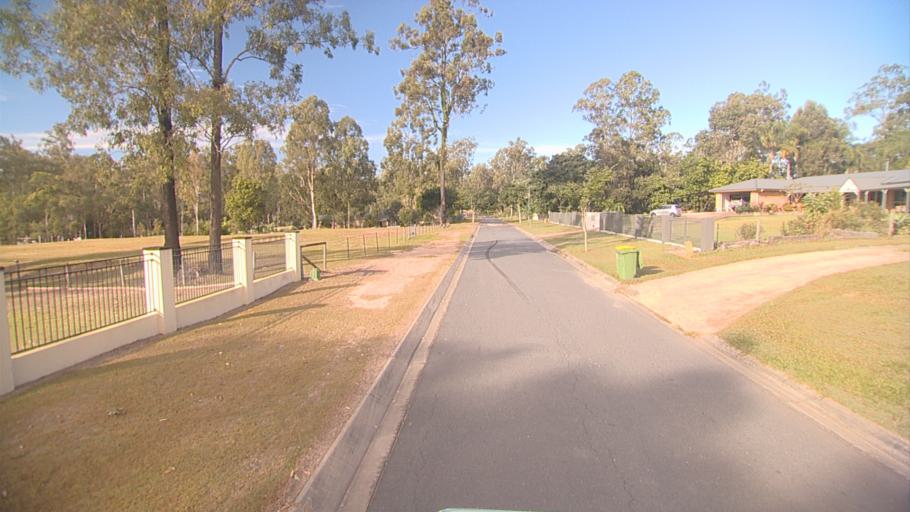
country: AU
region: Queensland
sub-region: Brisbane
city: Forest Lake
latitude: -27.6653
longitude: 152.9932
